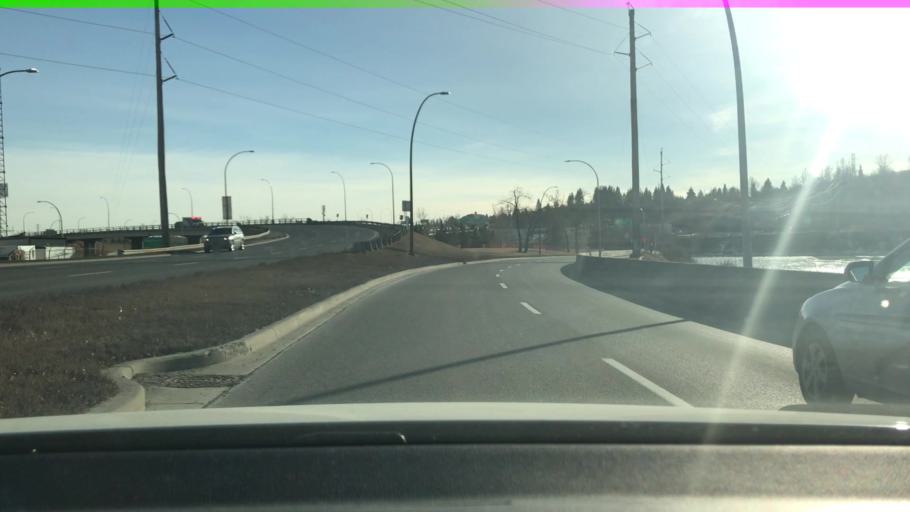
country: CA
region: Alberta
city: Calgary
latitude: 51.0510
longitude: -114.1191
